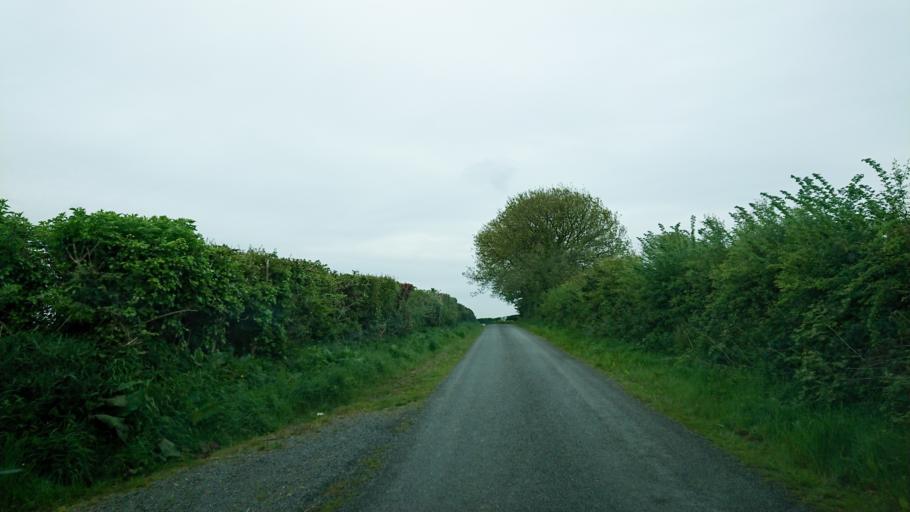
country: IE
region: Munster
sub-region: Waterford
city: Dunmore East
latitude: 52.2224
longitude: -7.0068
